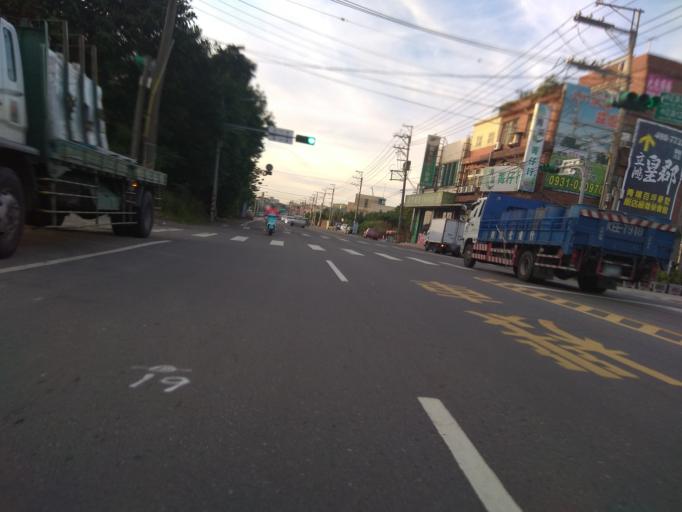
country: TW
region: Taiwan
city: Taoyuan City
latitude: 24.9707
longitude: 121.2016
